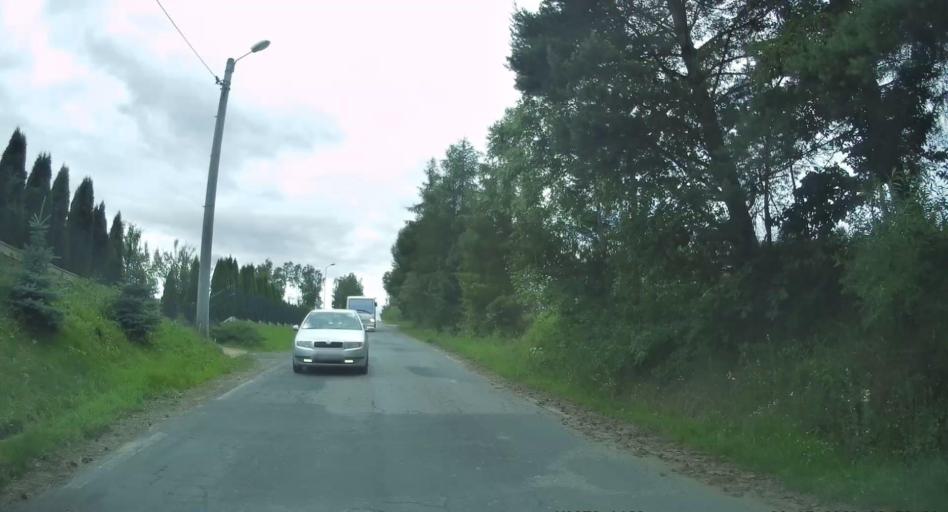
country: PL
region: Lesser Poland Voivodeship
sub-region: Powiat nowosadecki
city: Muszyna
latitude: 49.3900
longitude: 20.9070
